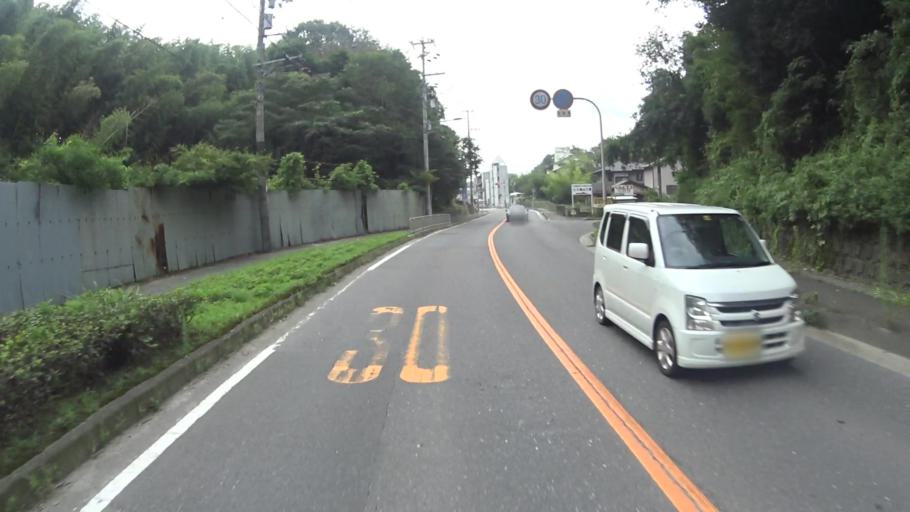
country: JP
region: Kyoto
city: Tanabe
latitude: 34.8076
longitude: 135.7238
